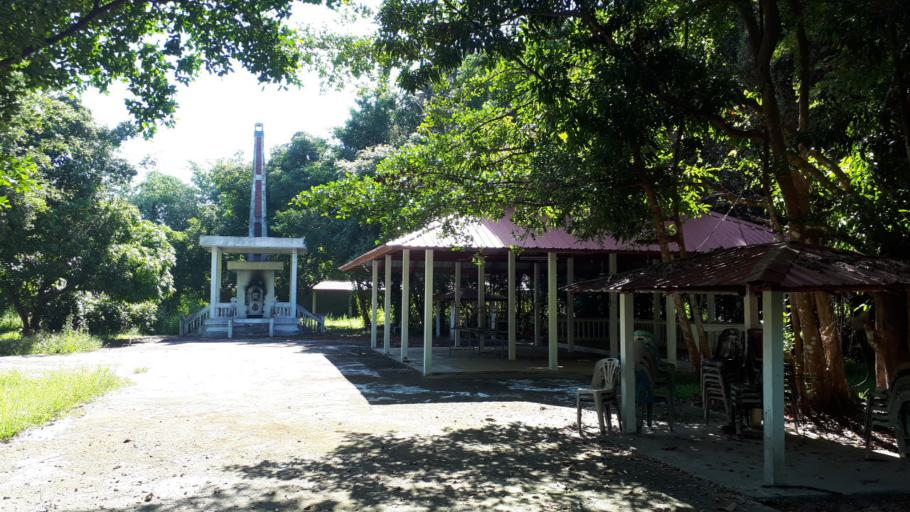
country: TH
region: Changwat Ubon Ratchathani
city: Warin Chamrap
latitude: 15.1339
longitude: 104.8466
